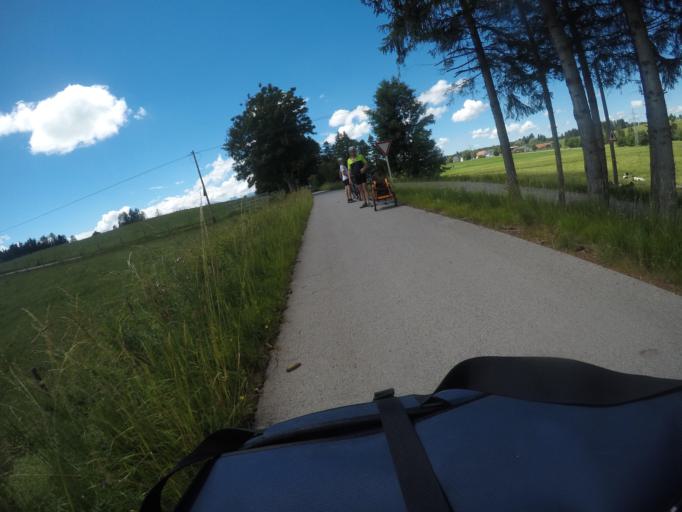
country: DE
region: Bavaria
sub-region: Swabia
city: Lechbruck
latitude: 47.6847
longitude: 10.7595
